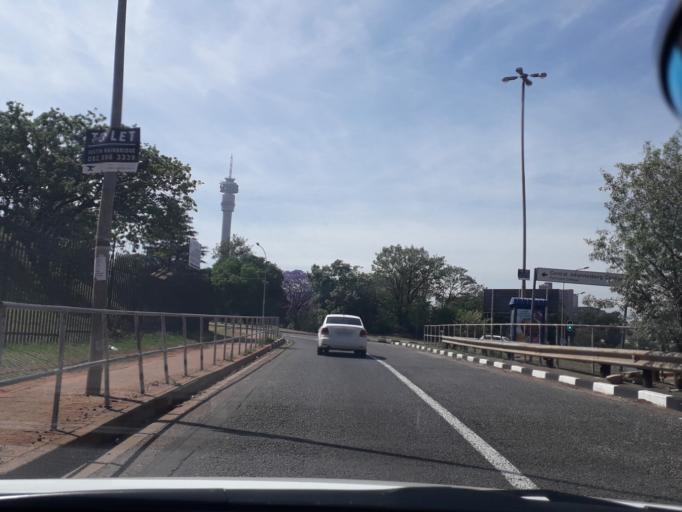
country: ZA
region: Gauteng
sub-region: City of Johannesburg Metropolitan Municipality
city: Johannesburg
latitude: -26.1817
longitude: 28.0395
